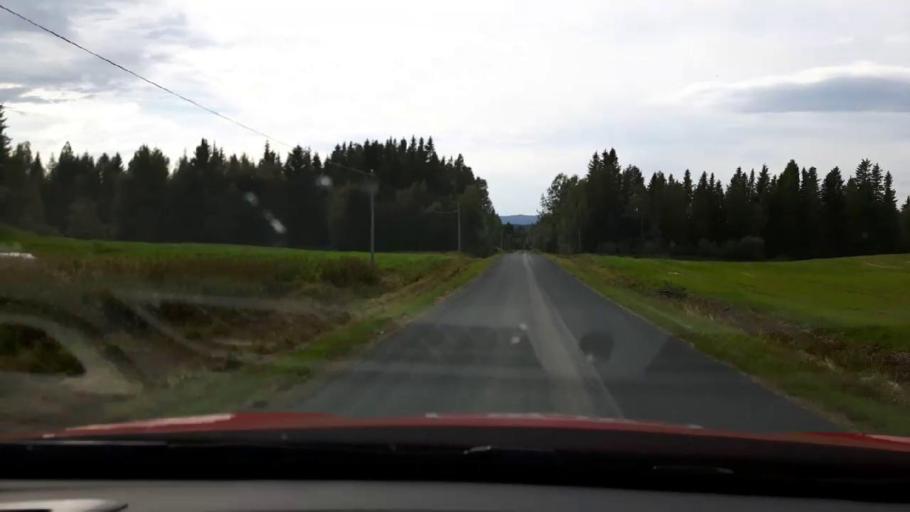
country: SE
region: Jaemtland
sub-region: Krokoms Kommun
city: Valla
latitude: 63.2690
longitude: 13.8542
